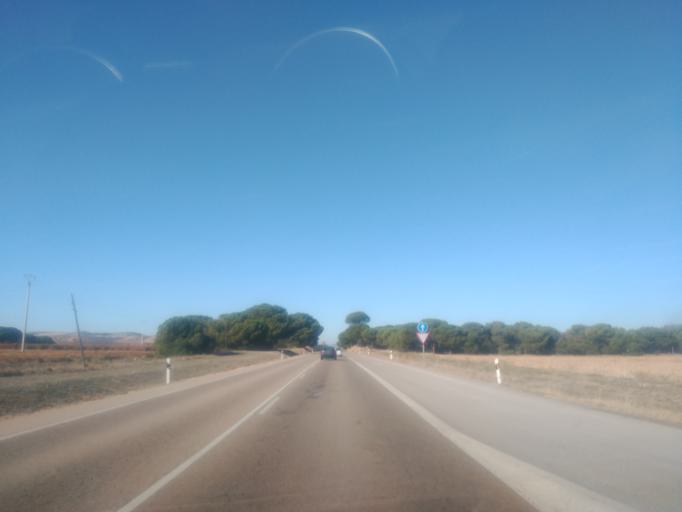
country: ES
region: Castille and Leon
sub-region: Provincia de Valladolid
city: Manzanillo
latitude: 41.6128
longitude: -4.1761
